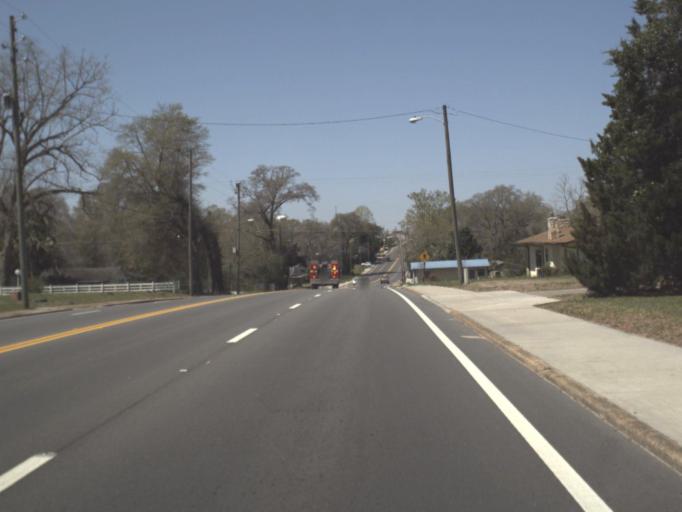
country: US
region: Florida
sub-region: Walton County
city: DeFuniak Springs
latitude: 30.7208
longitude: -86.1046
